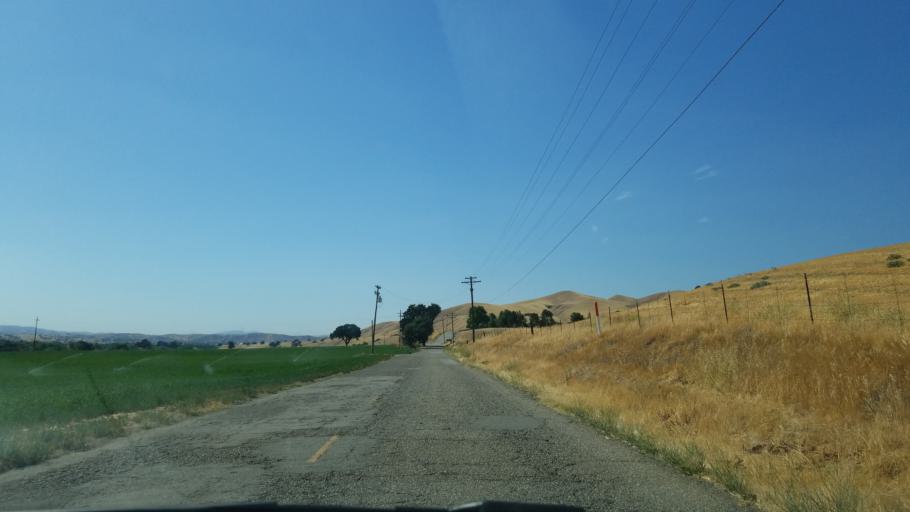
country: US
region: California
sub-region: San Luis Obispo County
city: San Miguel
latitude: 35.7705
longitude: -120.6903
